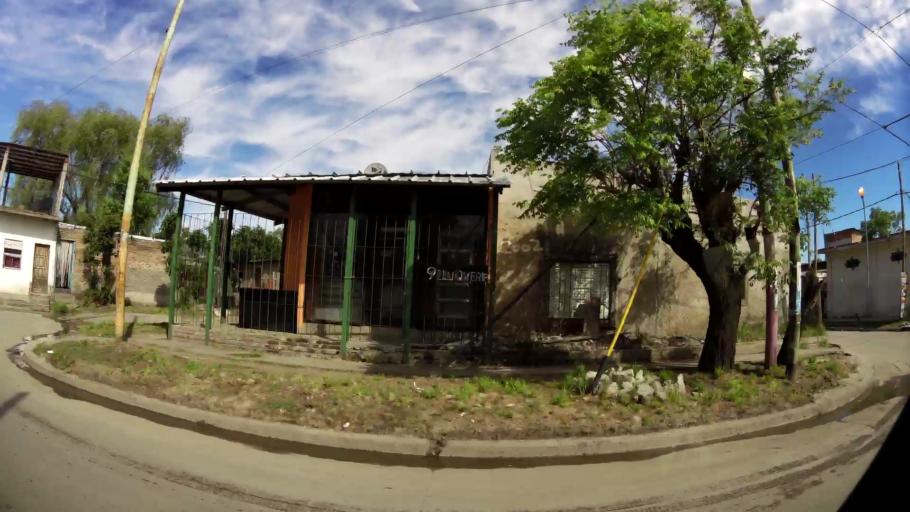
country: AR
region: Buenos Aires
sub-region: Partido de Quilmes
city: Quilmes
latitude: -34.7793
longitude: -58.3022
